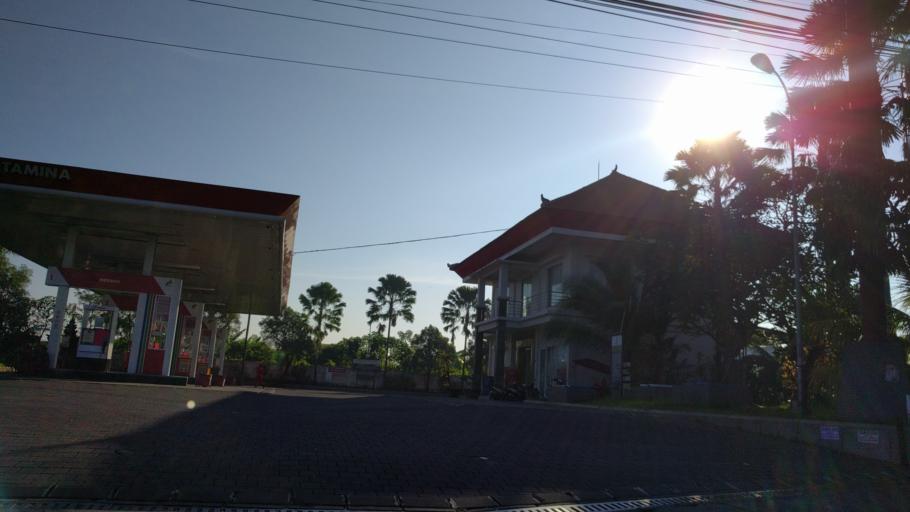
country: ID
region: Bali
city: Kuta
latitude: -8.6989
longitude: 115.1778
